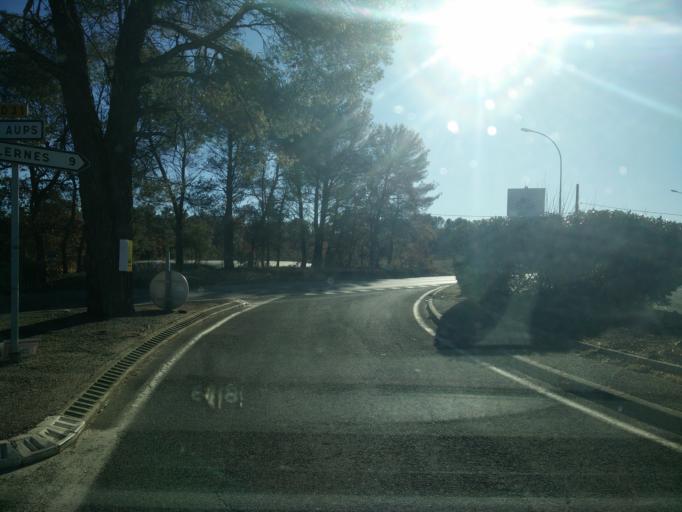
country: FR
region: Provence-Alpes-Cote d'Azur
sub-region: Departement du Var
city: Aups
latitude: 43.6155
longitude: 6.2192
